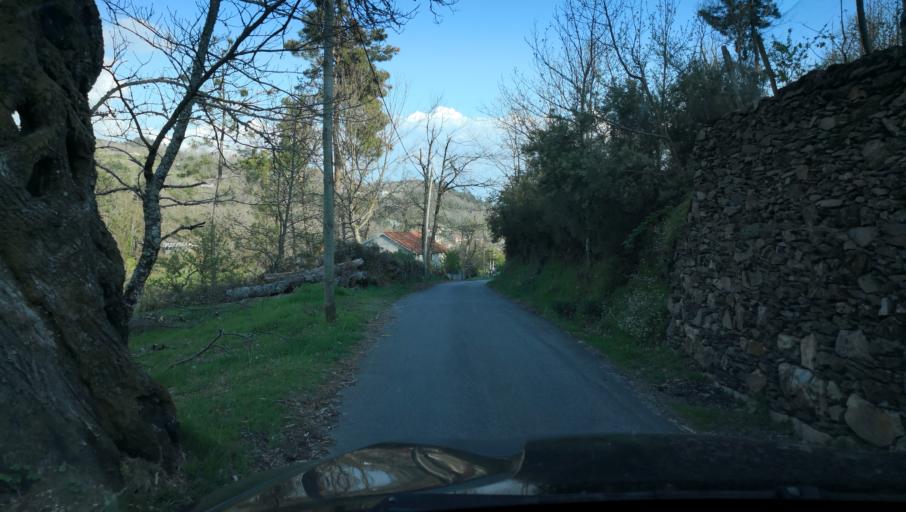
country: PT
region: Vila Real
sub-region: Vila Real
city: Vila Real
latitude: 41.3020
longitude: -7.8391
